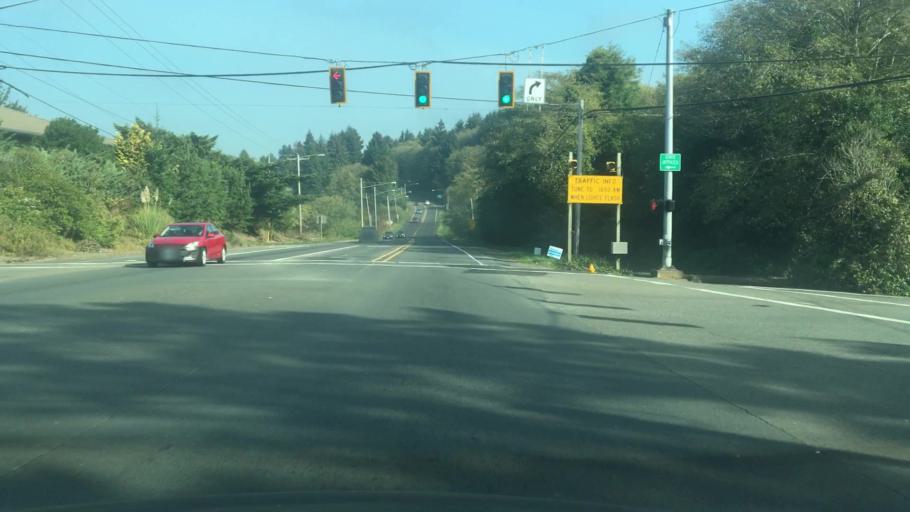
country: US
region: Oregon
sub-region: Lincoln County
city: Lincoln City
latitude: 44.9976
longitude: -123.9968
